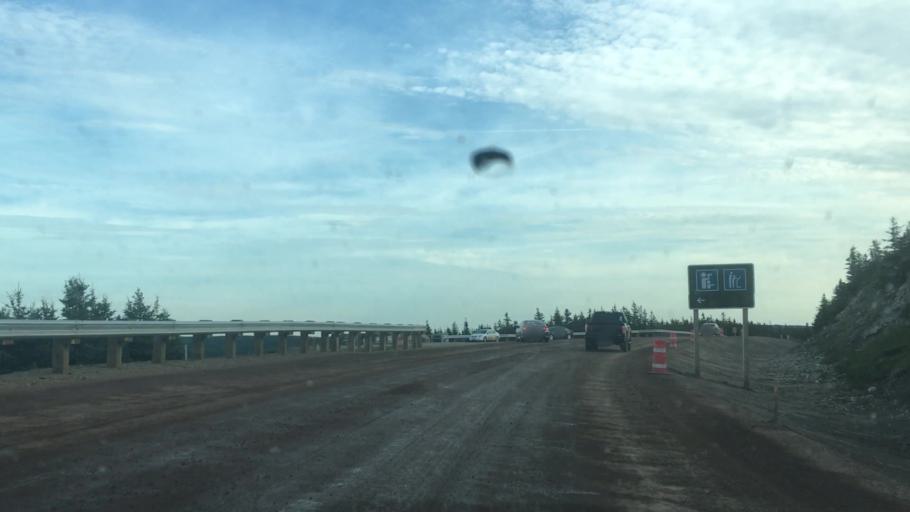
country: CA
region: Nova Scotia
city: Sydney Mines
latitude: 46.8040
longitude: -60.8436
